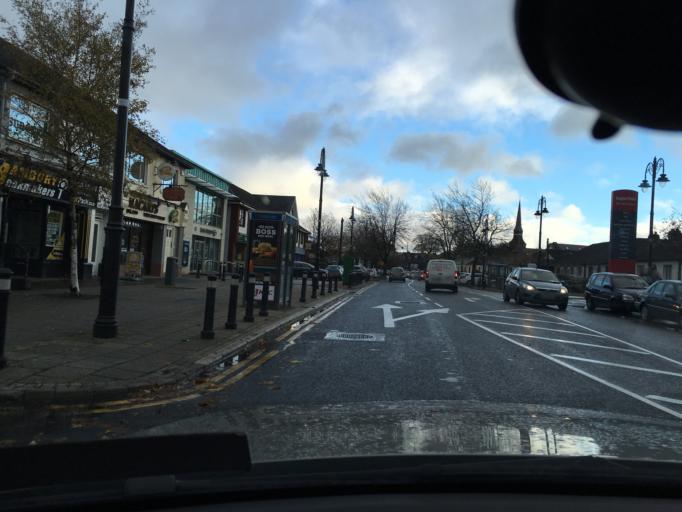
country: IE
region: Leinster
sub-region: Fingal County
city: Blanchardstown
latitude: 53.3871
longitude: -6.3778
